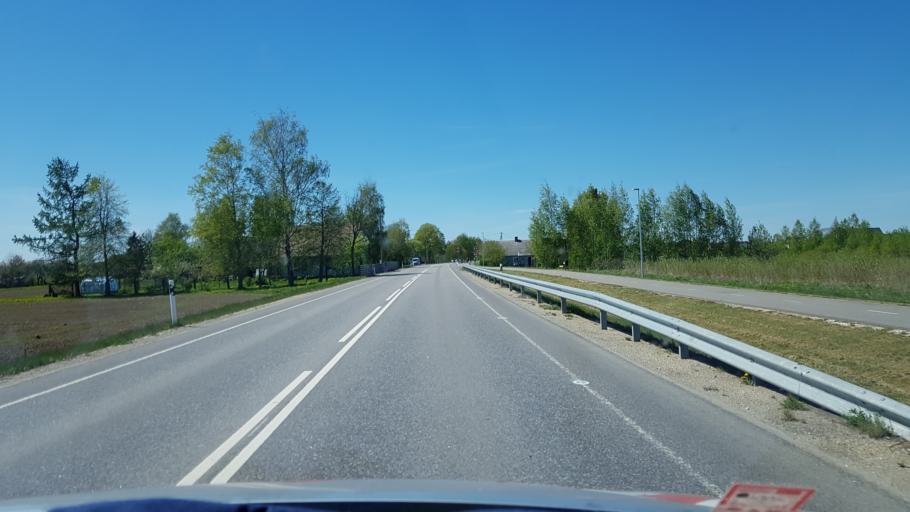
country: EE
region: Tartu
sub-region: UElenurme vald
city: Ulenurme
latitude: 58.3122
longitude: 26.7097
